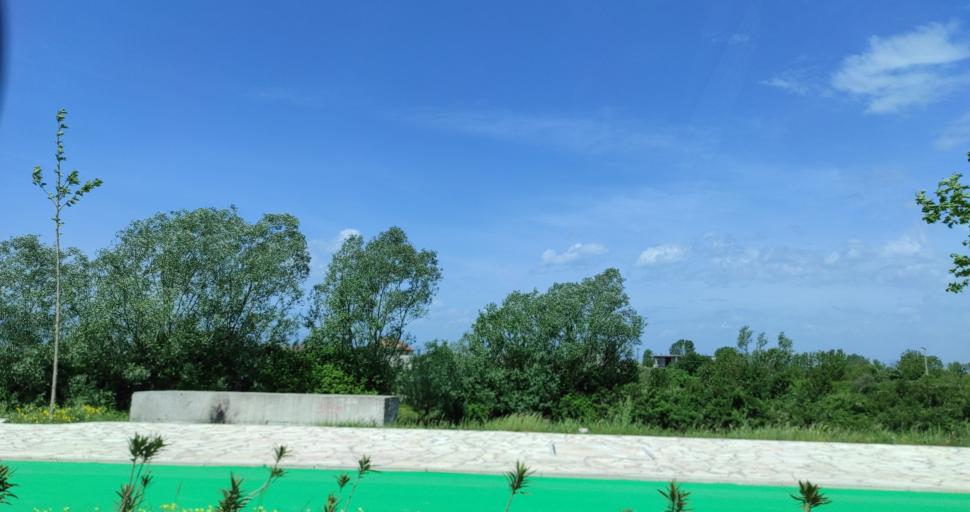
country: AL
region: Shkoder
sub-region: Rrethi i Shkodres
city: Shkoder
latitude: 42.0813
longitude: 19.4929
